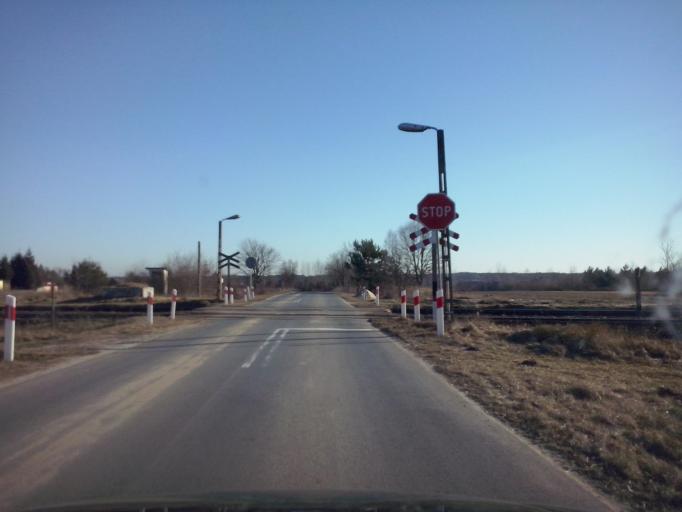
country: PL
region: Subcarpathian Voivodeship
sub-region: Powiat nizanski
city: Harasiuki
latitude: 50.5303
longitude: 22.4456
